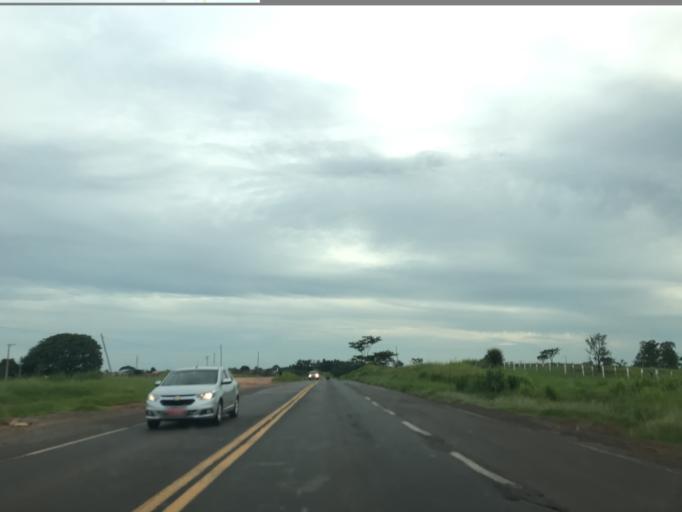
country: BR
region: Sao Paulo
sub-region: Tupa
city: Tupa
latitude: -21.6456
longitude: -50.5084
